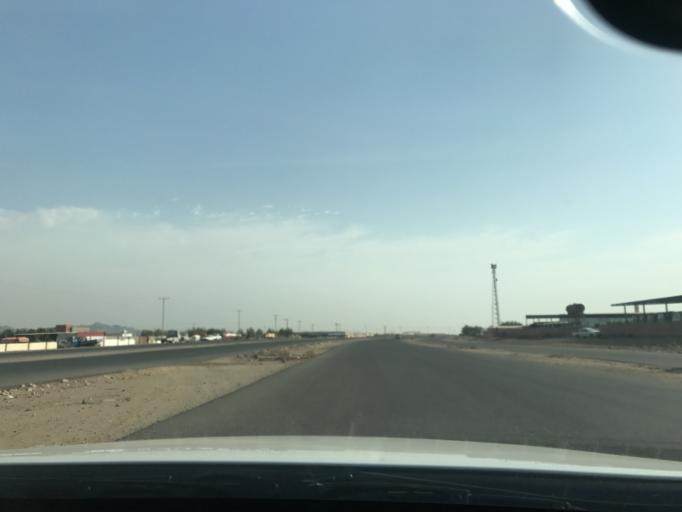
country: SA
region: Makkah
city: Al Jumum
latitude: 21.4468
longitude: 39.5196
